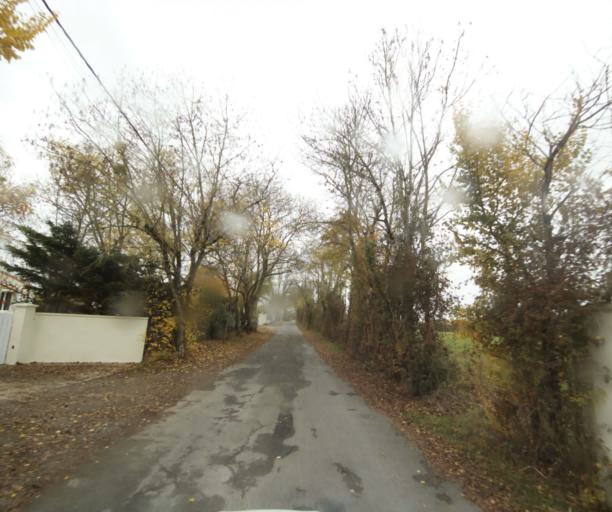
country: FR
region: Poitou-Charentes
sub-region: Departement de la Charente-Maritime
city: Saintes
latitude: 45.7641
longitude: -0.6279
